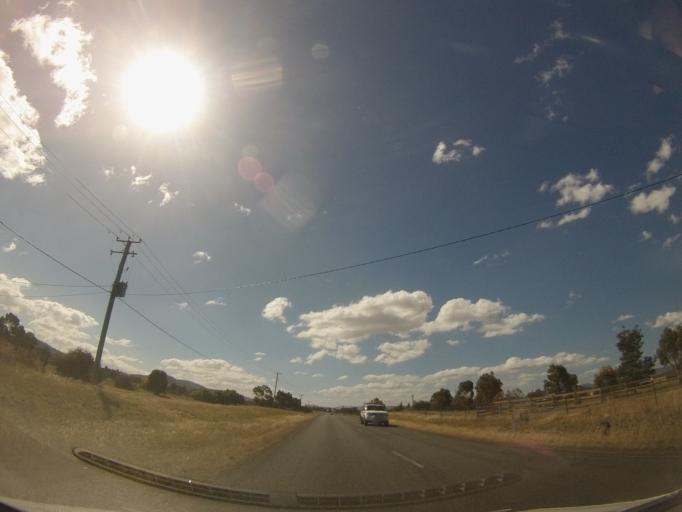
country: AU
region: Tasmania
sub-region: Clarence
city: Seven Mile Beach
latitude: -42.8525
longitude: 147.4862
